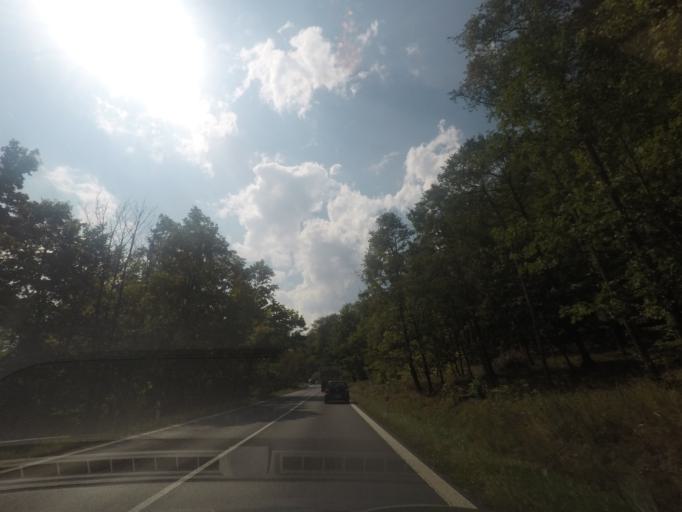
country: CZ
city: Kamenicky Senov
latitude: 50.7735
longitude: 14.5104
